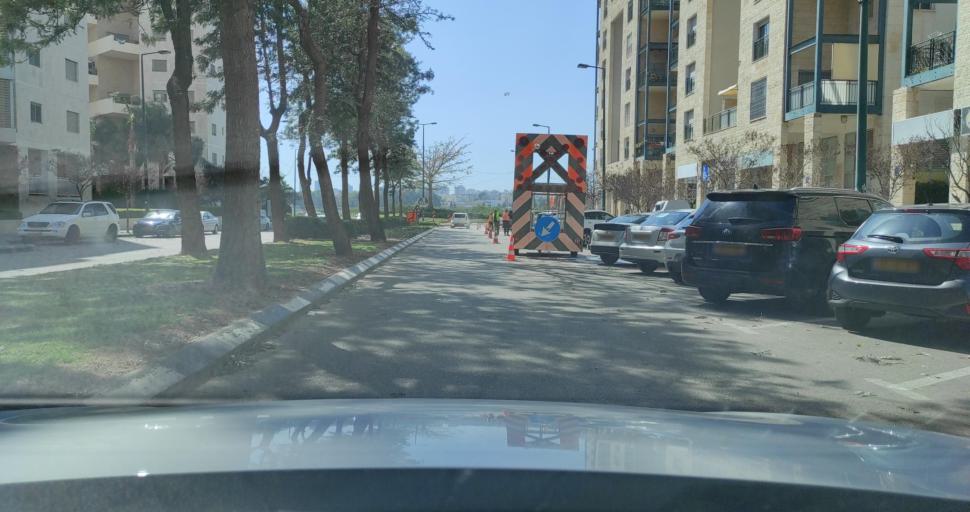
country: IL
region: Central District
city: Nordiyya
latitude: 32.3029
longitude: 34.8707
